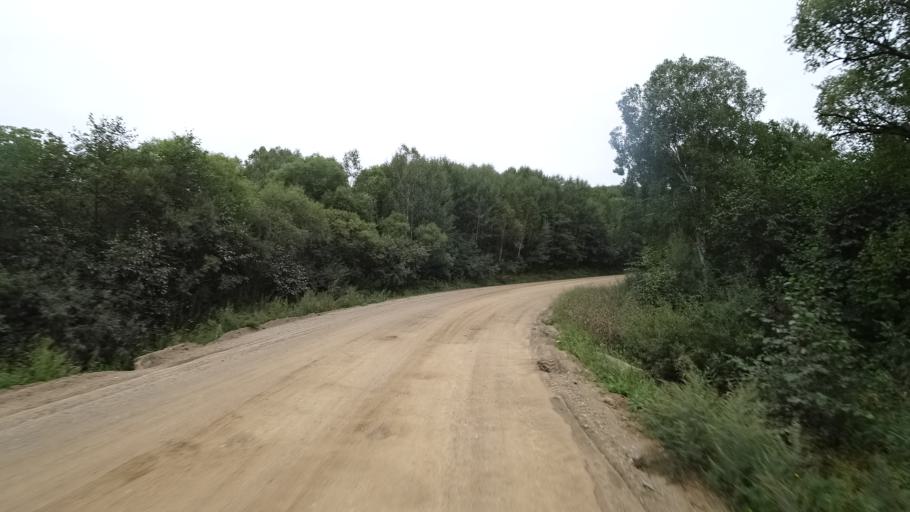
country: RU
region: Primorskiy
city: Rettikhovka
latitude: 44.1764
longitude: 132.8384
